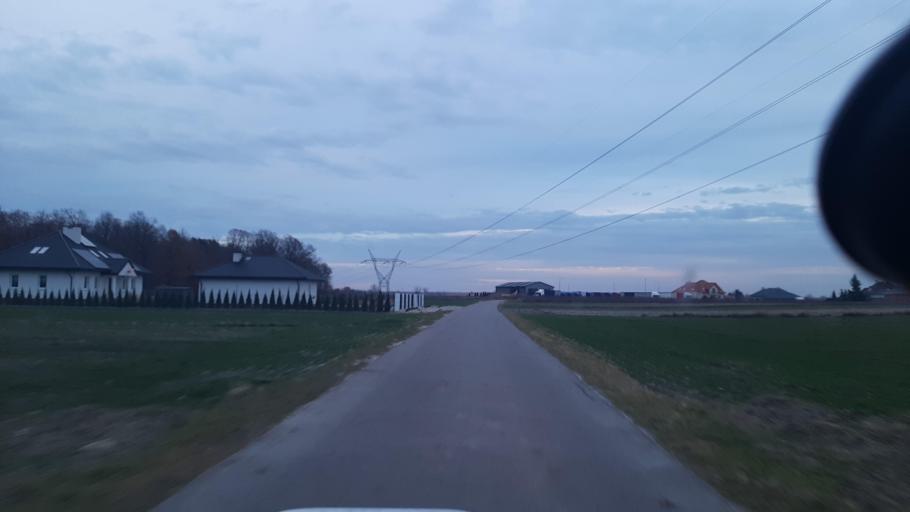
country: PL
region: Lublin Voivodeship
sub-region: Powiat lubelski
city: Garbow
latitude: 51.3701
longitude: 22.3827
